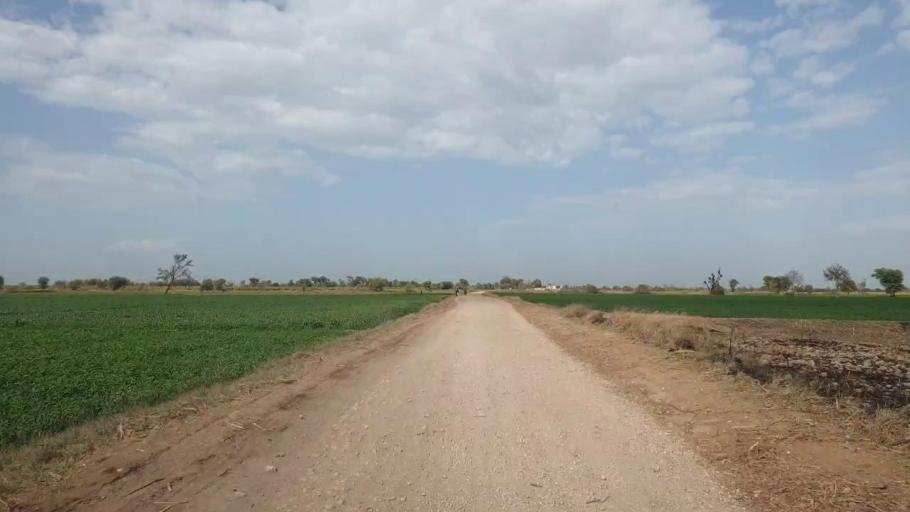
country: PK
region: Sindh
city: Shahdadpur
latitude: 25.9770
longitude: 68.4770
